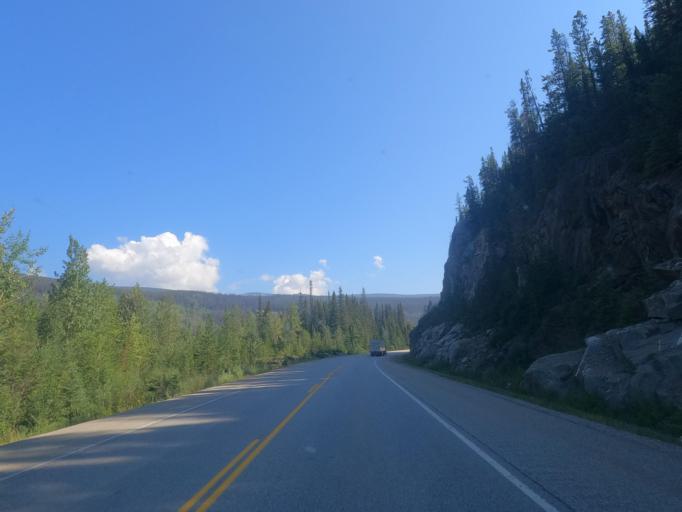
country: CA
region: Alberta
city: Jasper Park Lodge
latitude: 52.8861
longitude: -118.4828
